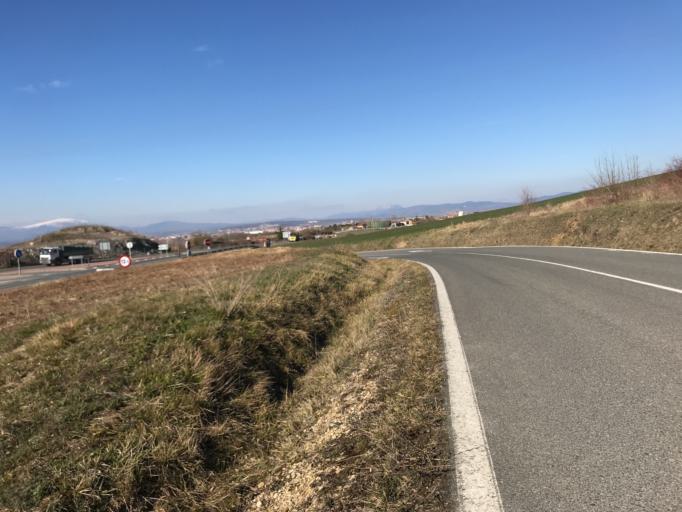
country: ES
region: Basque Country
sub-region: Provincia de Alava
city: Gasteiz / Vitoria
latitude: 42.8139
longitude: -2.6806
